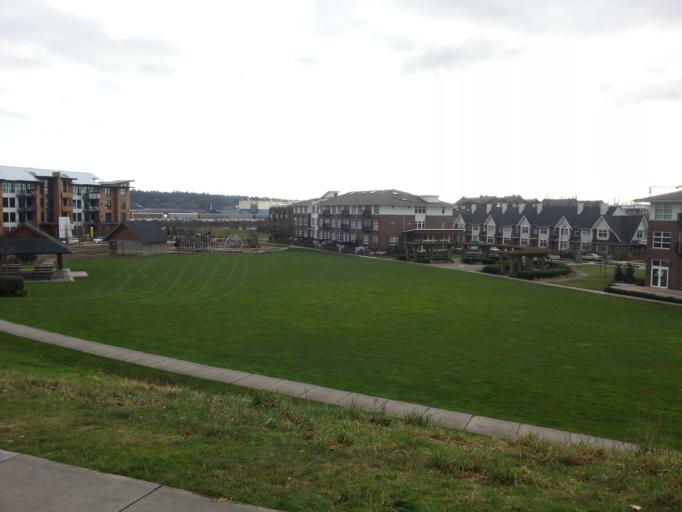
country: CA
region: British Columbia
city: New Westminster
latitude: 49.1954
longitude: -122.9237
